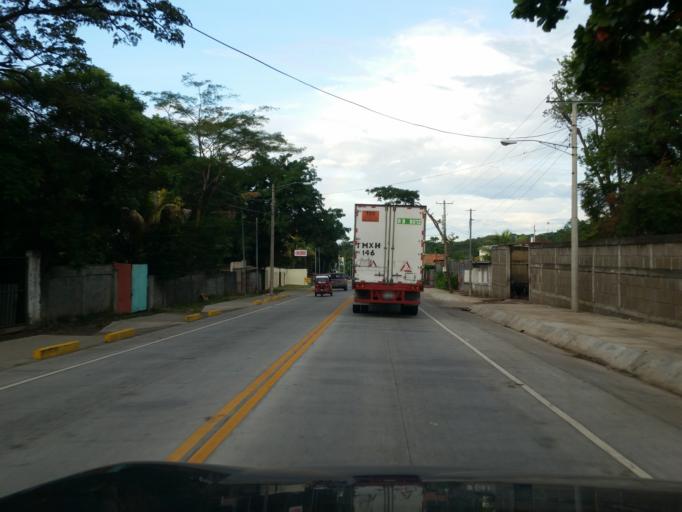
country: NI
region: Managua
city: Ciudad Sandino
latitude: 12.1041
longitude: -86.3328
